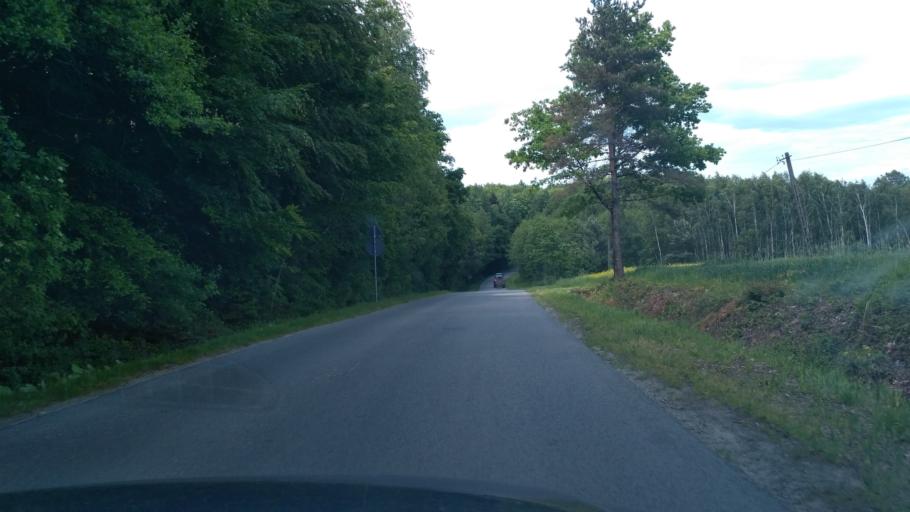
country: PL
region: Subcarpathian Voivodeship
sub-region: Powiat ropczycko-sedziszowski
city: Ropczyce
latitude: 50.0166
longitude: 21.6092
